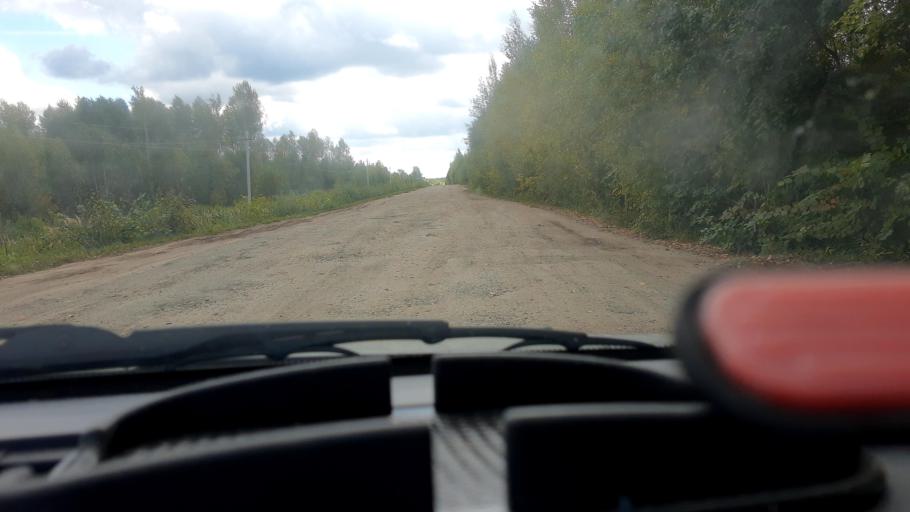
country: RU
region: Mariy-El
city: Kilemary
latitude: 56.8945
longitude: 46.7511
